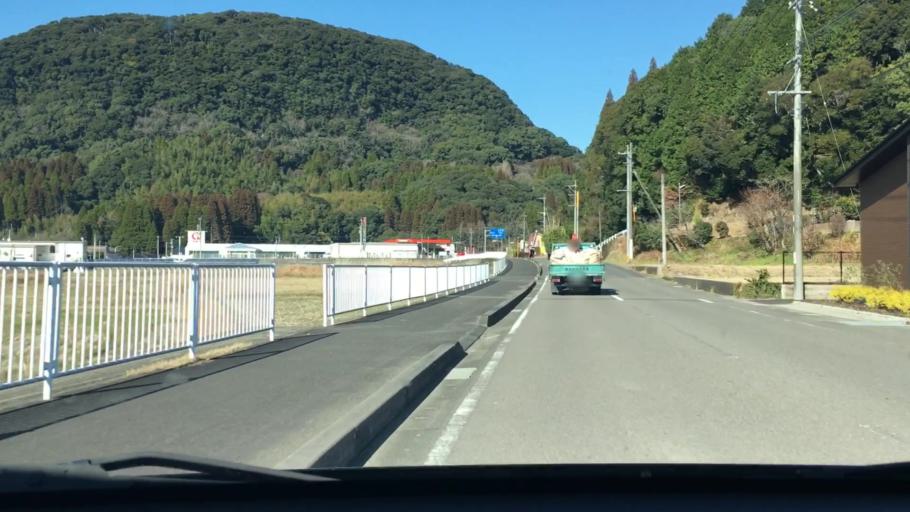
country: JP
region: Kagoshima
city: Satsumasendai
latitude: 31.7952
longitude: 130.4104
